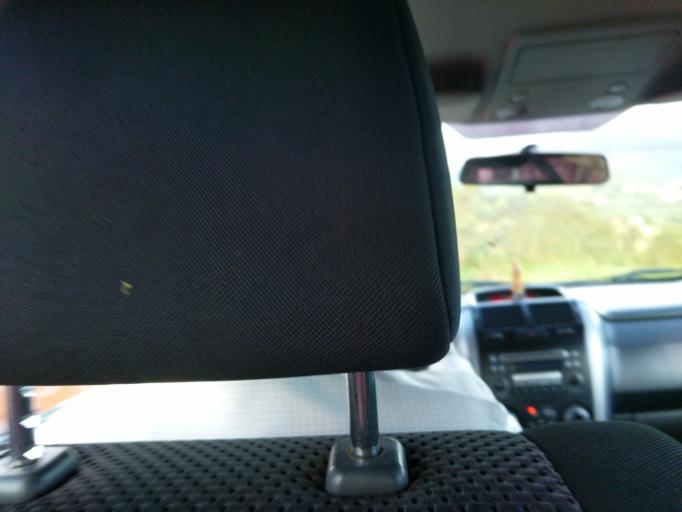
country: RW
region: Kigali
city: Kigali
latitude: -2.0126
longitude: 30.0395
